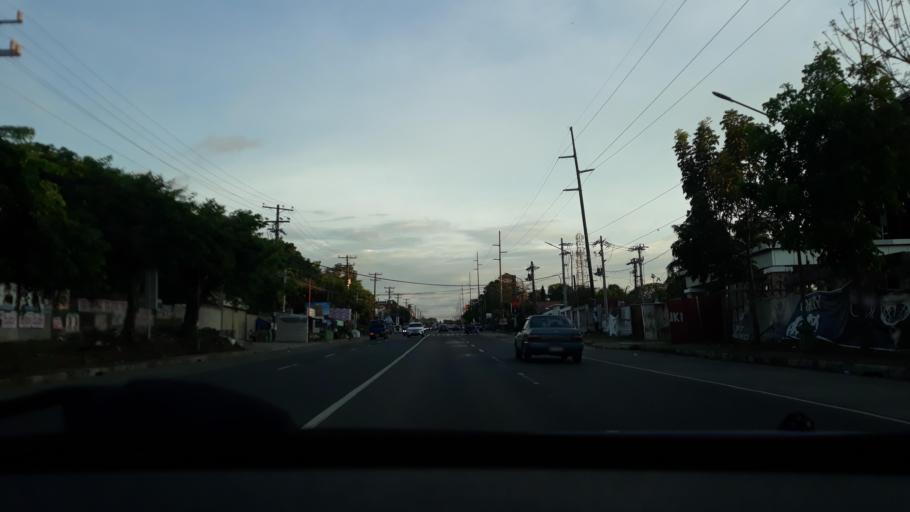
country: PH
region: Calabarzon
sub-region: Province of Cavite
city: Silang
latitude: 14.2209
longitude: 120.9683
